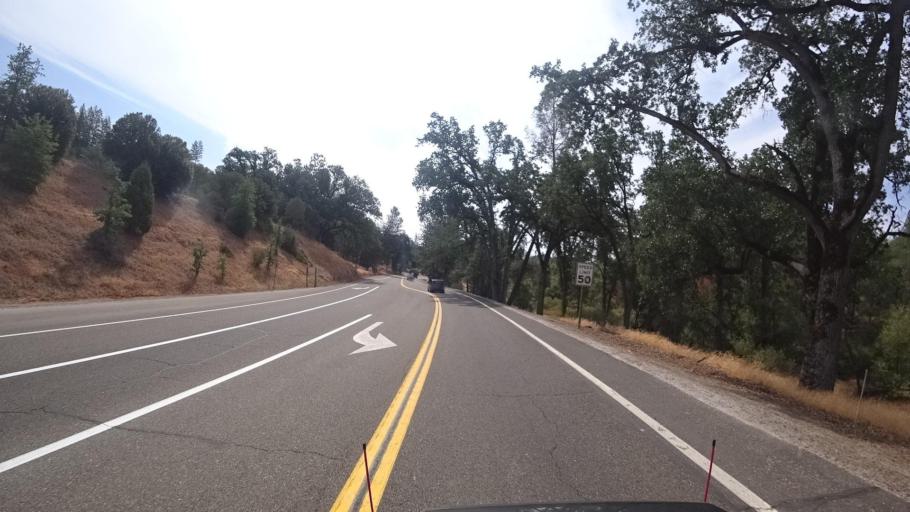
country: US
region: California
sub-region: Mariposa County
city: Midpines
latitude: 37.5607
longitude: -119.9354
